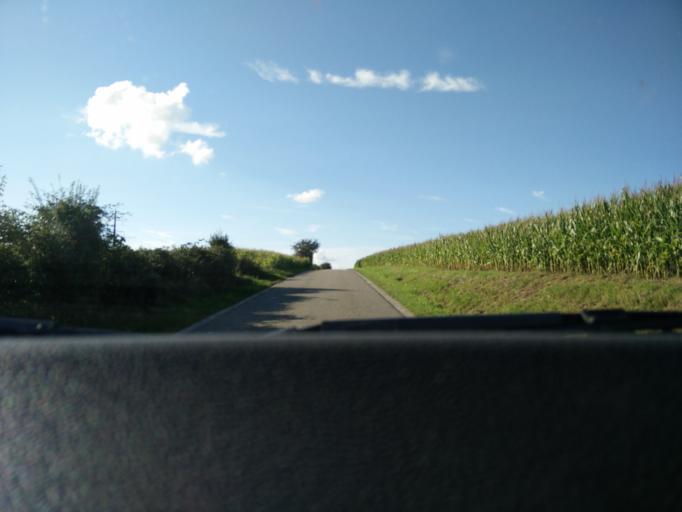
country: BE
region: Wallonia
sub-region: Province du Hainaut
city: Beaumont
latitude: 50.2046
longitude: 4.2603
